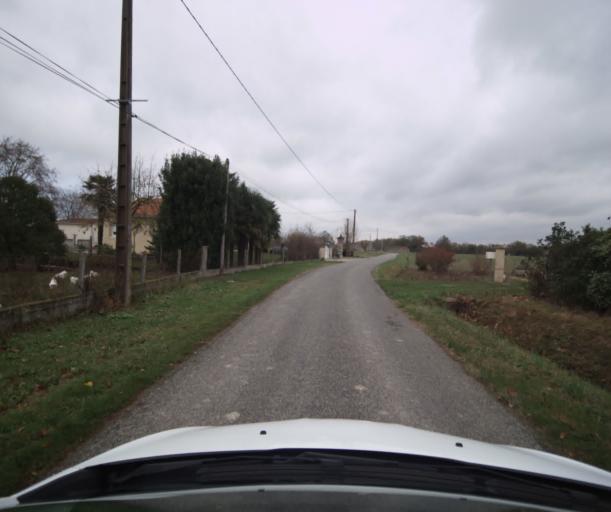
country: FR
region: Midi-Pyrenees
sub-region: Departement du Tarn-et-Garonne
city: Saint-Porquier
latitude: 44.0541
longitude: 1.1613
